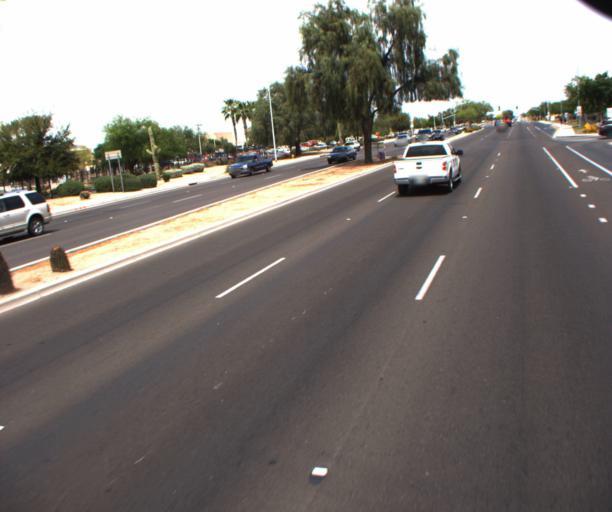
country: US
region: Arizona
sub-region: Maricopa County
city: Sun Lakes
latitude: 33.2489
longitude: -111.8411
